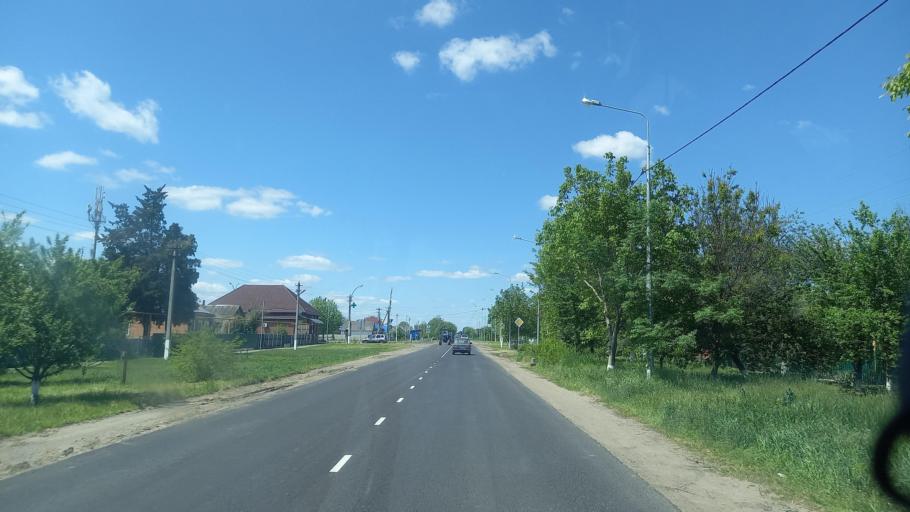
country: RU
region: Krasnodarskiy
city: Tbilisskaya
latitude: 45.3264
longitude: 40.2545
